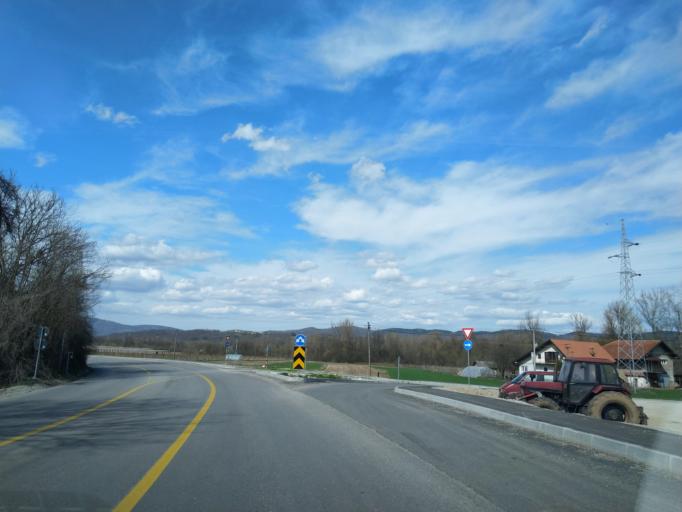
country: RS
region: Central Serbia
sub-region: Zlatiborski Okrug
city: Arilje
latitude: 43.7851
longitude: 20.1088
